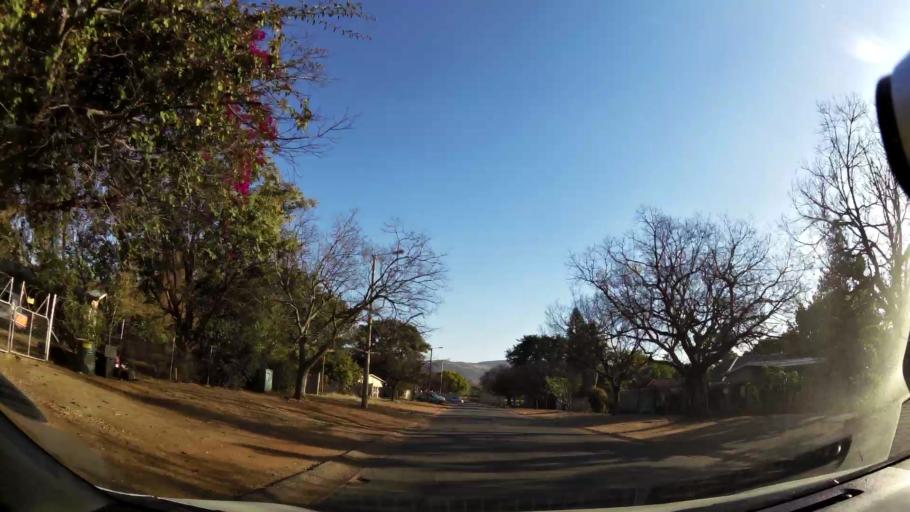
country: ZA
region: North-West
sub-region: Bojanala Platinum District Municipality
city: Rustenburg
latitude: -25.6829
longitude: 27.2239
